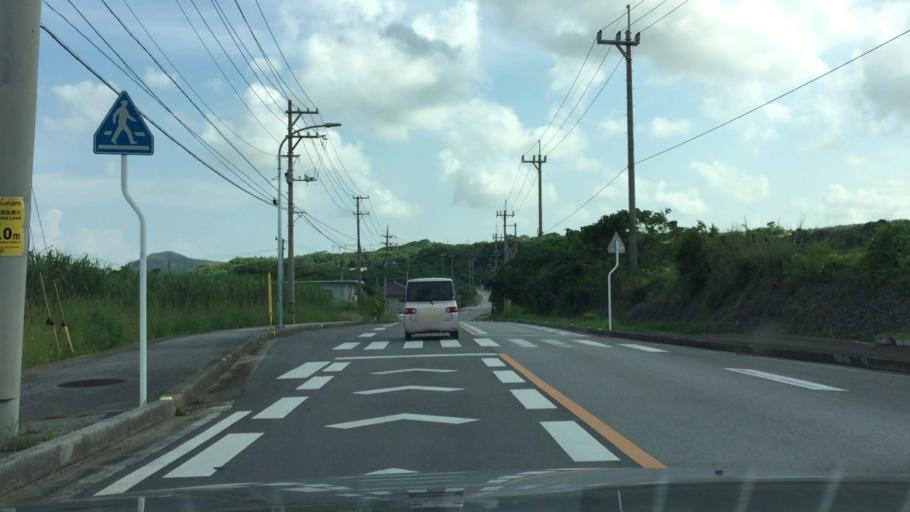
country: JP
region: Okinawa
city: Ishigaki
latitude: 24.4344
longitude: 124.2486
